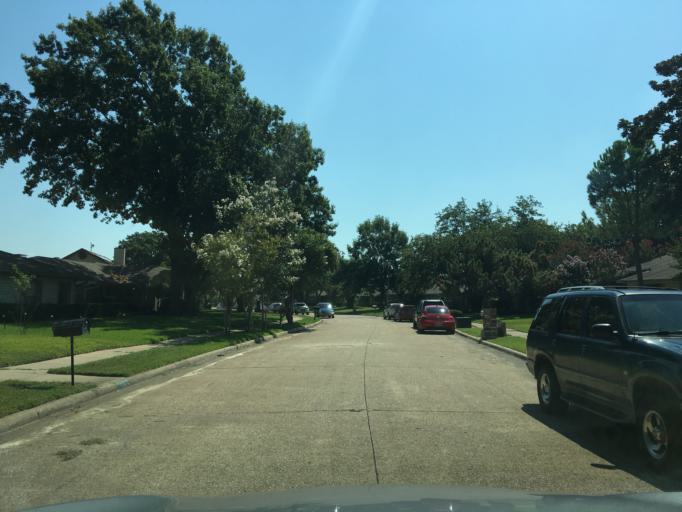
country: US
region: Texas
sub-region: Dallas County
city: Garland
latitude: 32.9355
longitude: -96.6505
